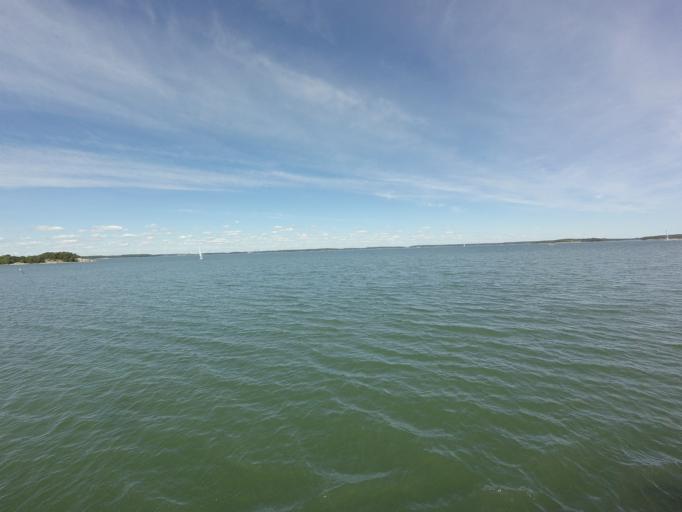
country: FI
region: Varsinais-Suomi
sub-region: Turku
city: Naantali
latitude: 60.3769
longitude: 22.0746
